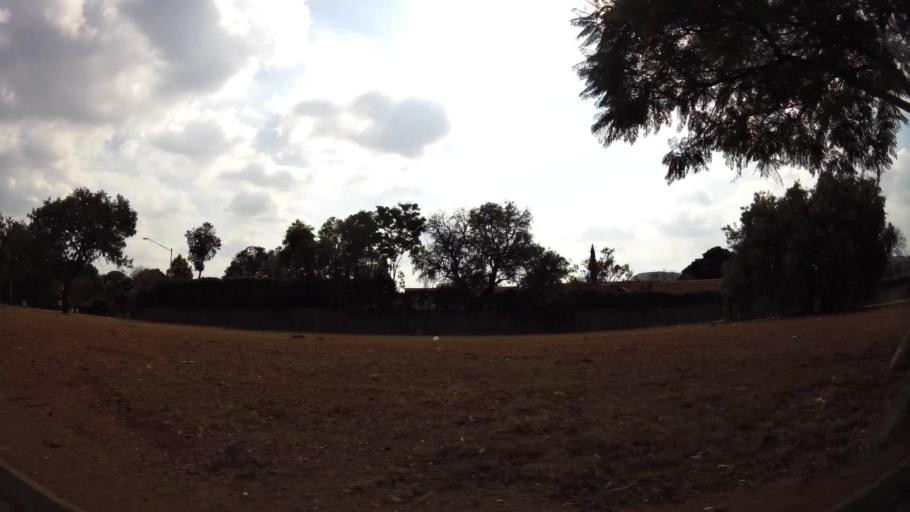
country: ZA
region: Gauteng
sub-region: City of Tshwane Metropolitan Municipality
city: Pretoria
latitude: -25.7837
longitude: 28.2959
